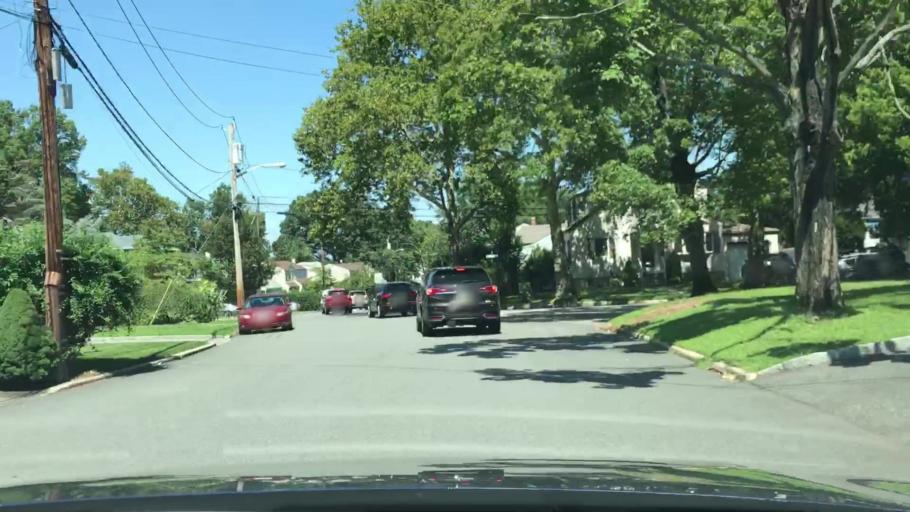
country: US
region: New Jersey
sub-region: Bergen County
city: Teaneck
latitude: 40.9150
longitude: -74.0155
